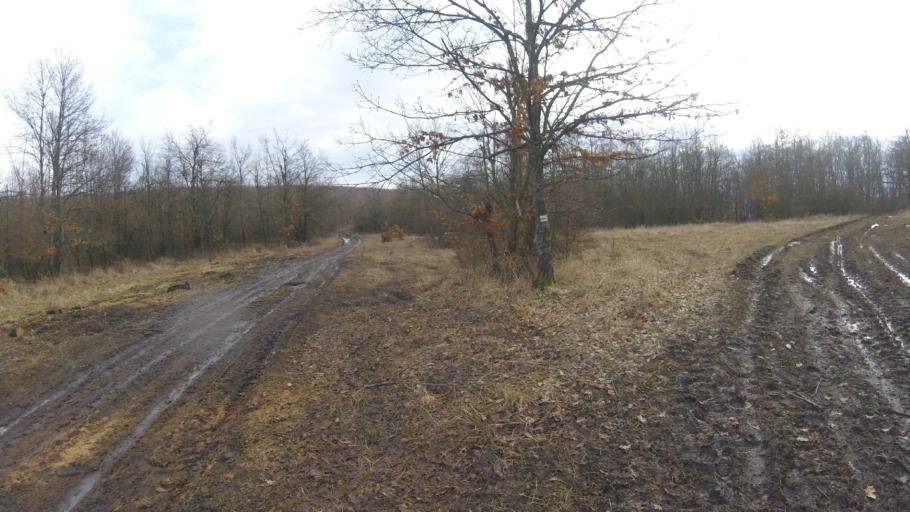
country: HU
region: Pest
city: Pilisszentkereszt
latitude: 47.6978
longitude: 18.9310
